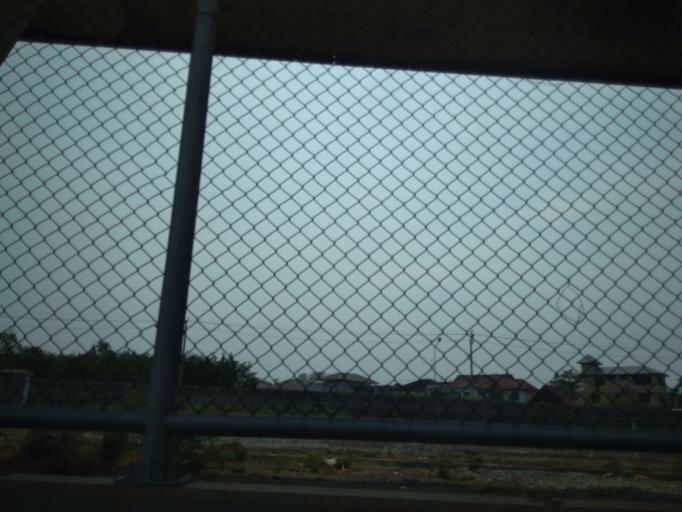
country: TH
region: Bangkok
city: Taling Chan
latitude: 13.7925
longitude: 100.4365
